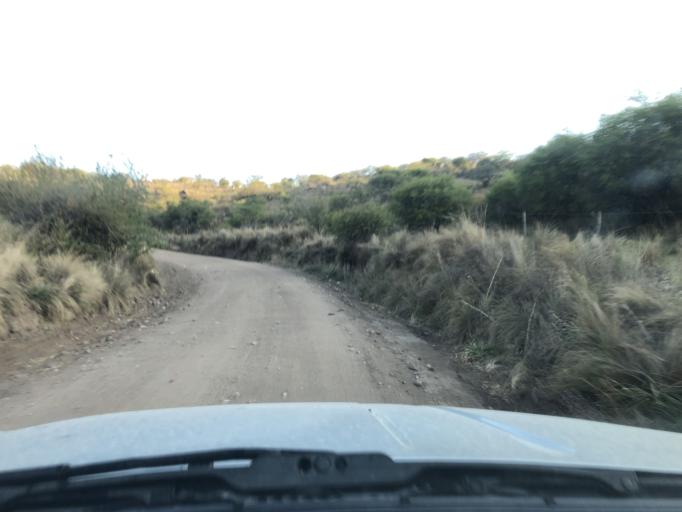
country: AR
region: Cordoba
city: Agua de Oro
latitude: -31.0568
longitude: -64.3519
